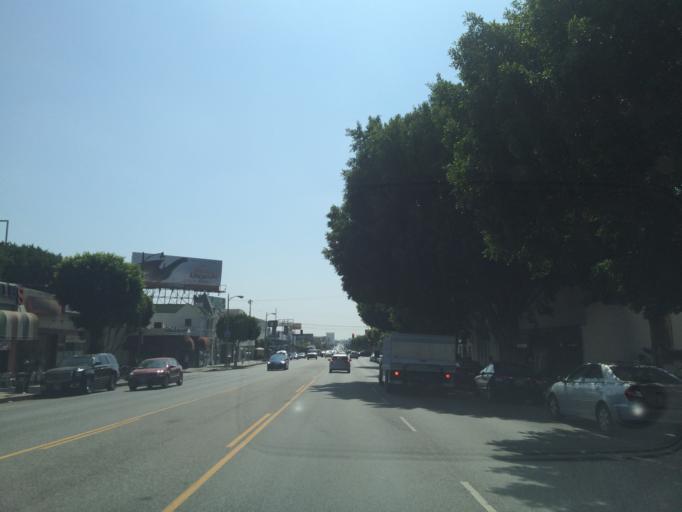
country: US
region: California
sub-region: Los Angeles County
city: Beverly Hills
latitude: 34.0551
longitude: -118.3855
